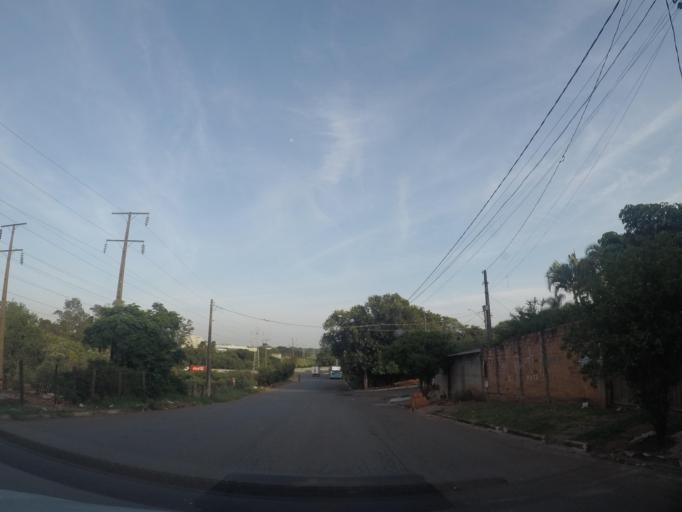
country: BR
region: Sao Paulo
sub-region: Hortolandia
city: Hortolandia
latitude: -22.8472
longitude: -47.1698
